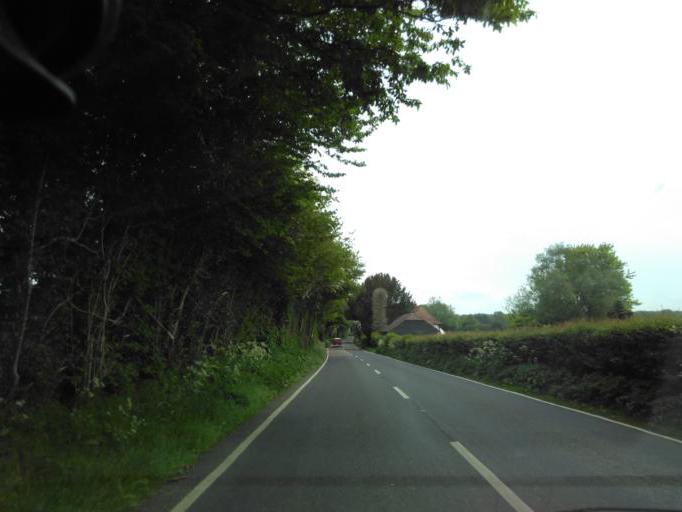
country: GB
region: England
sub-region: Kent
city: Chartham
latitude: 51.1990
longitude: 1.0568
